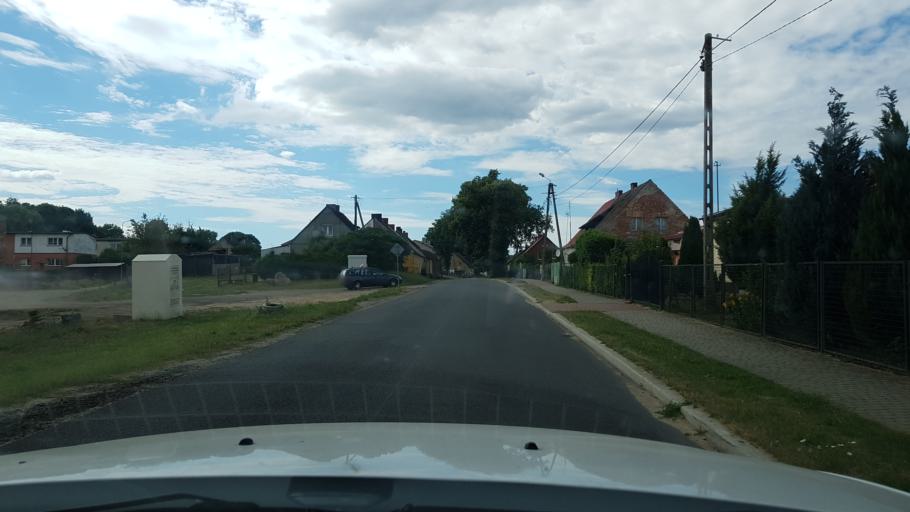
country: PL
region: West Pomeranian Voivodeship
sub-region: Powiat drawski
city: Wierzchowo
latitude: 53.4774
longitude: 16.0564
